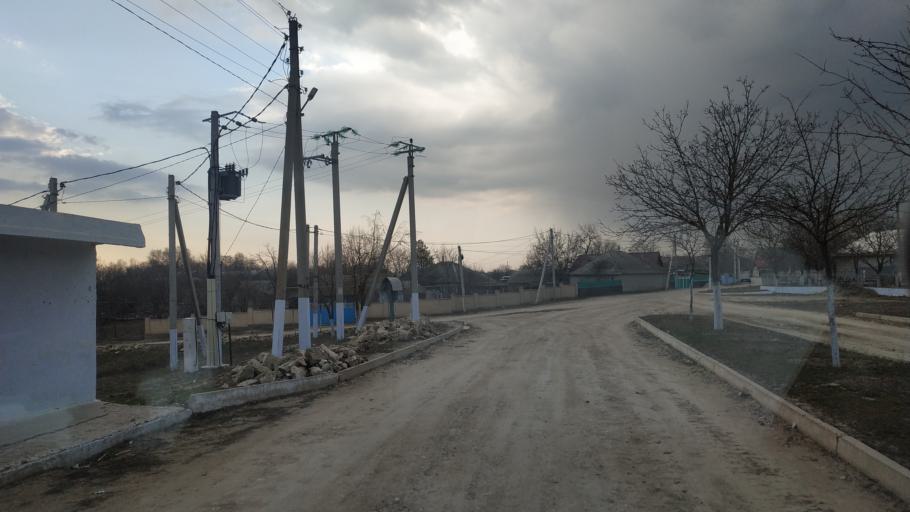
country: MD
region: Telenesti
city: Grigoriopol
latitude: 47.0244
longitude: 29.3498
